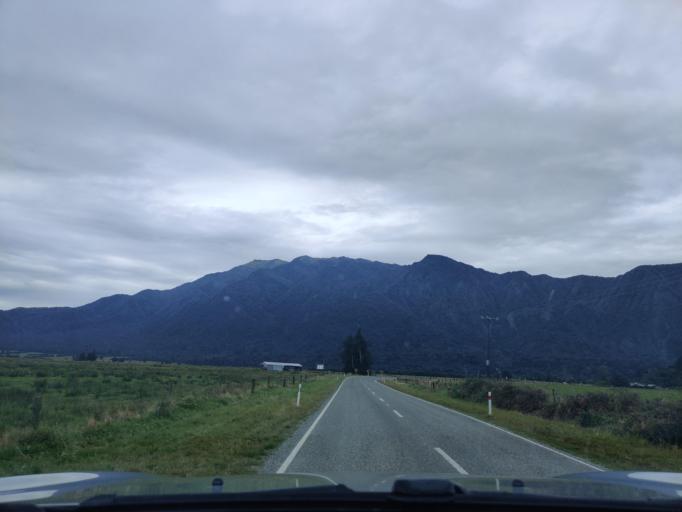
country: NZ
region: West Coast
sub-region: Westland District
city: Hokitika
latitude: -43.1533
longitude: 170.6088
